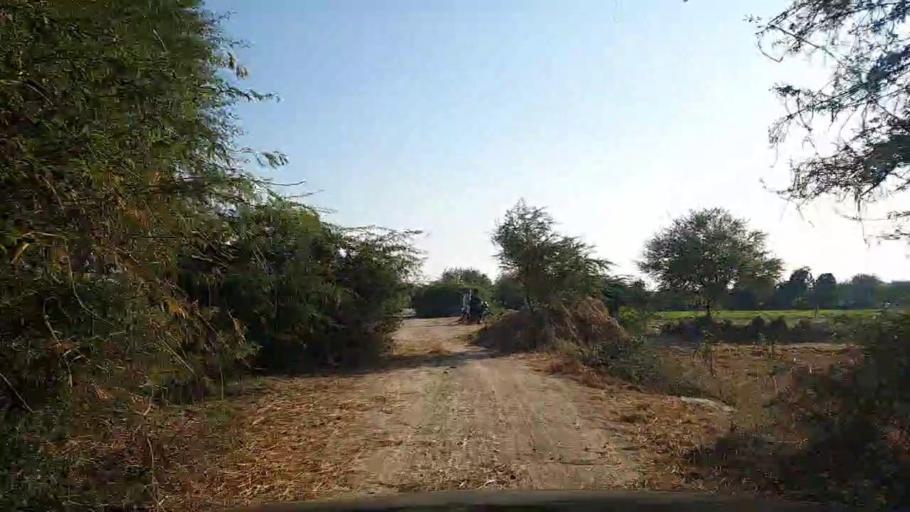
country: PK
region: Sindh
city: Mirpur Batoro
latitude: 24.6754
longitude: 68.3644
